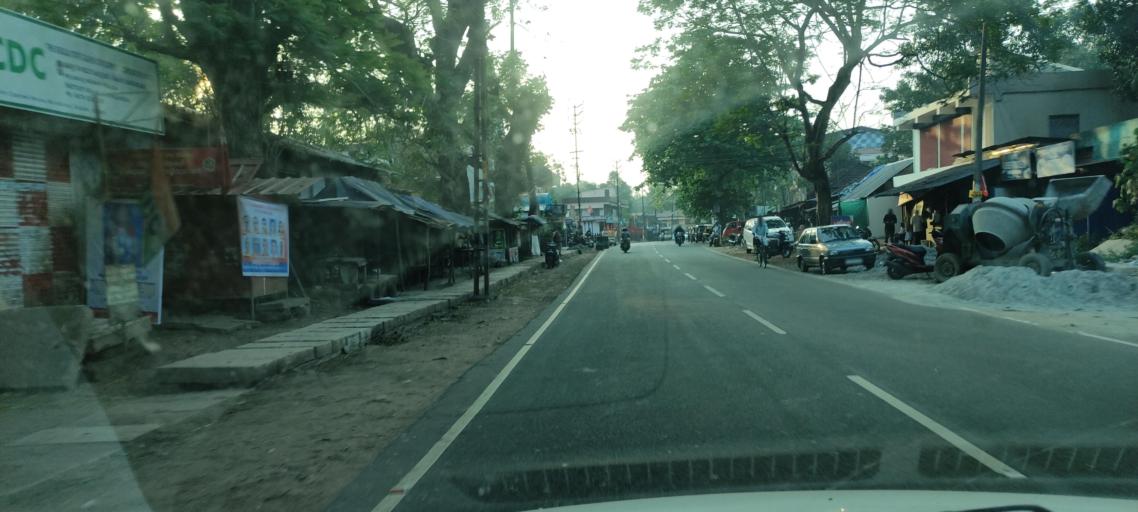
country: IN
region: Kerala
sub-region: Alappuzha
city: Kattanam
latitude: 9.1720
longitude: 76.5967
